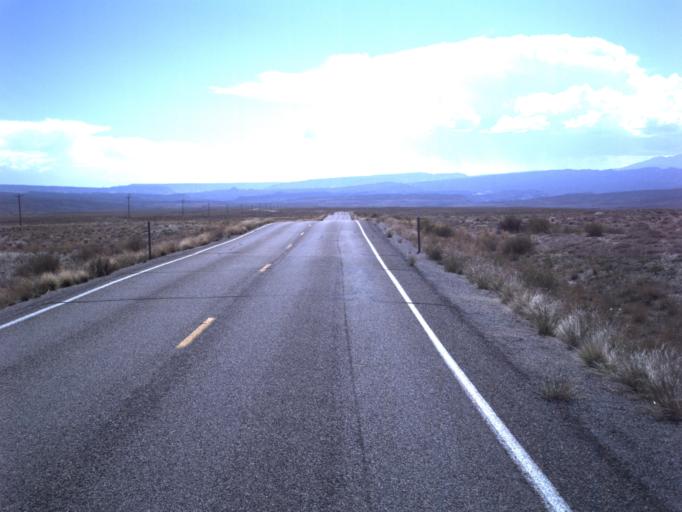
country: US
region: Utah
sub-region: Grand County
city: Moab
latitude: 38.9251
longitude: -109.3385
